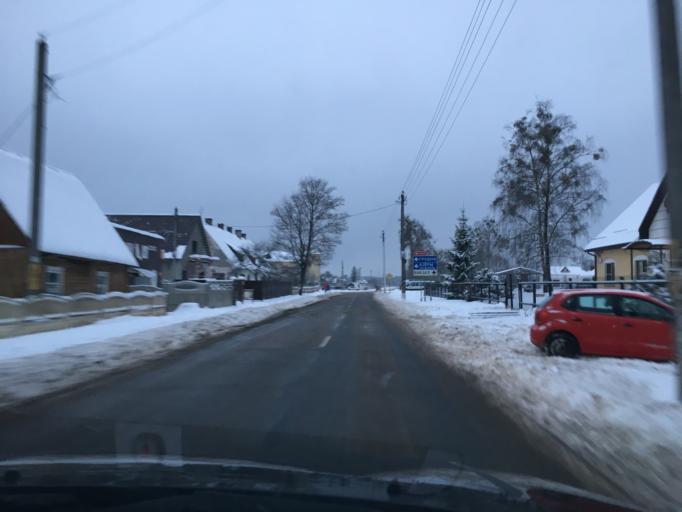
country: LT
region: Alytaus apskritis
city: Druskininkai
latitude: 53.8865
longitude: 24.1363
